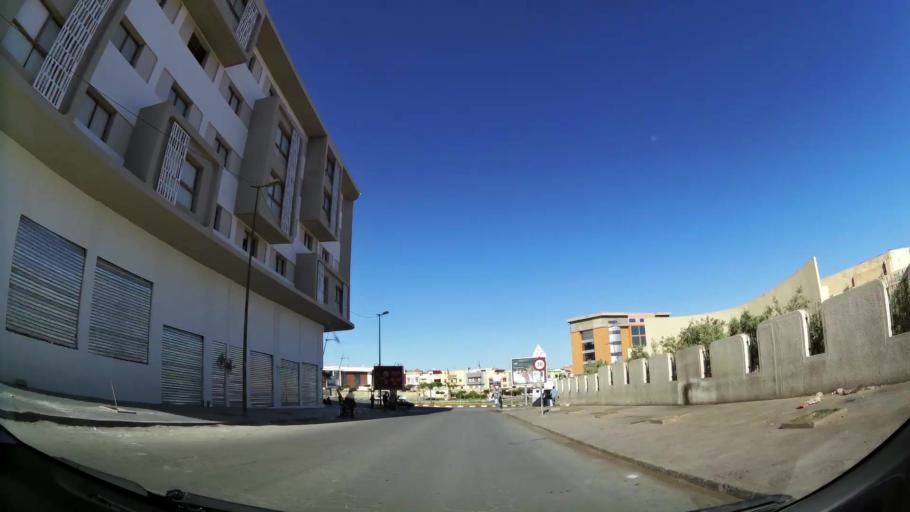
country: MA
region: Oriental
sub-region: Oujda-Angad
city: Oujda
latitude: 34.6562
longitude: -1.8990
